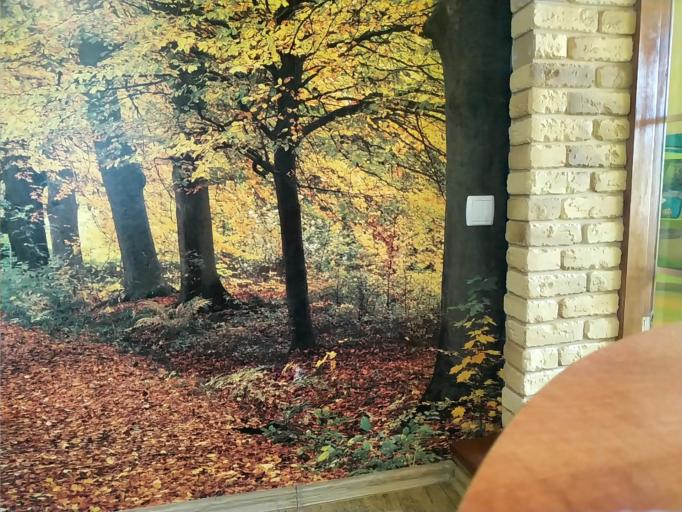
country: RU
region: Arkhangelskaya
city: Onega
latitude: 63.7047
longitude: 38.0883
